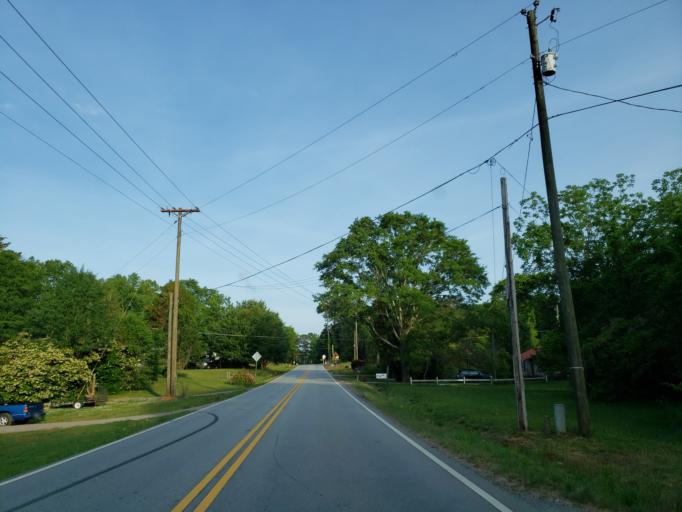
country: US
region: Georgia
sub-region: Carroll County
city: Carrollton
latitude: 33.5912
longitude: -85.1225
